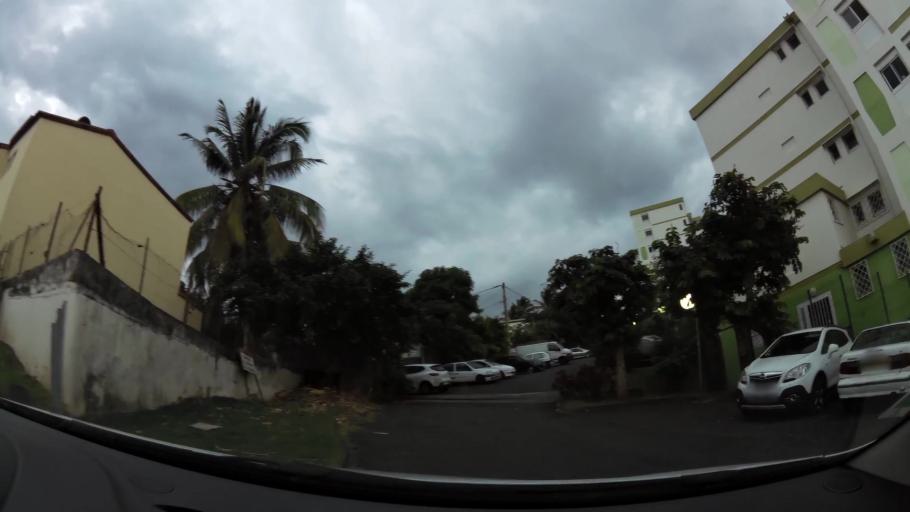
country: RE
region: Reunion
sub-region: Reunion
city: Saint-Denis
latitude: -20.8982
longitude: 55.4706
